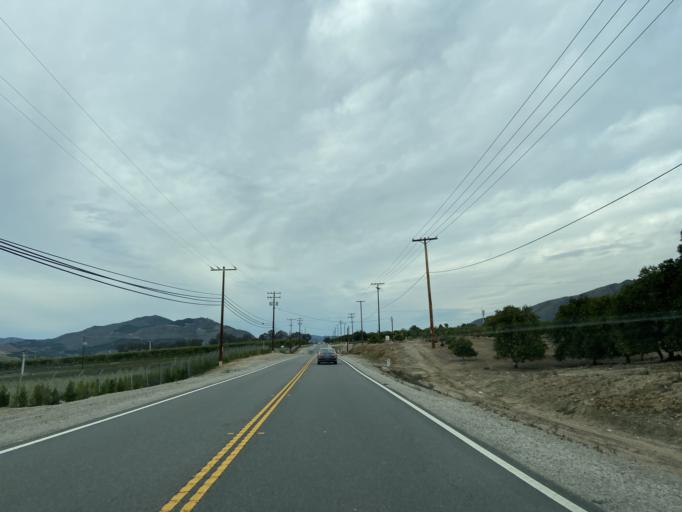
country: US
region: California
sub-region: San Diego County
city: Valley Center
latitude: 33.3091
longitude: -116.9841
